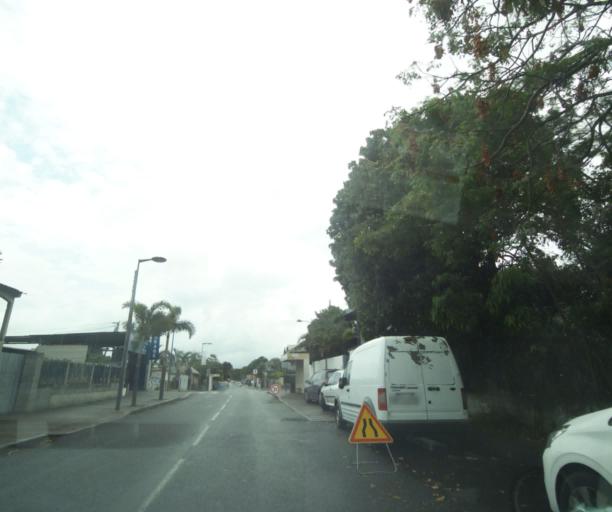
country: RE
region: Reunion
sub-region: Reunion
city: Saint-Paul
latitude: -21.0059
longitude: 55.2770
